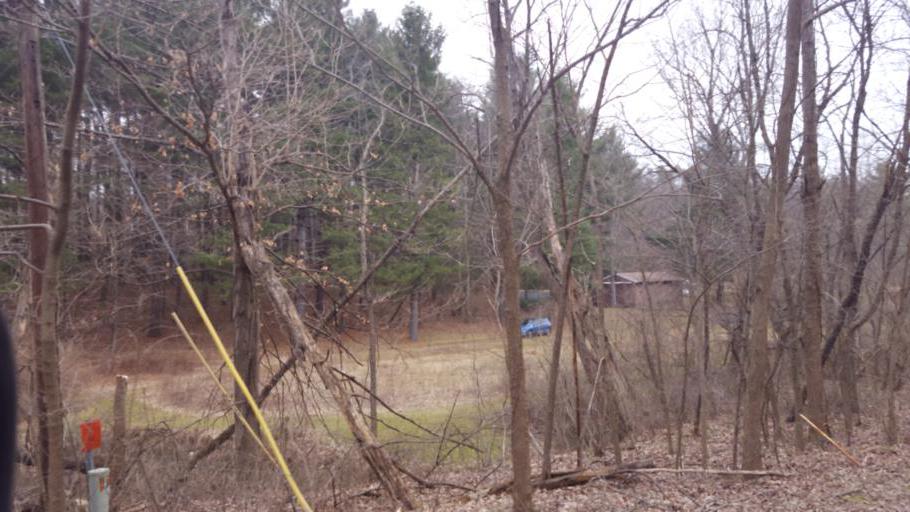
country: US
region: Ohio
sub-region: Ashland County
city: Loudonville
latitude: 40.5693
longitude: -82.2472
